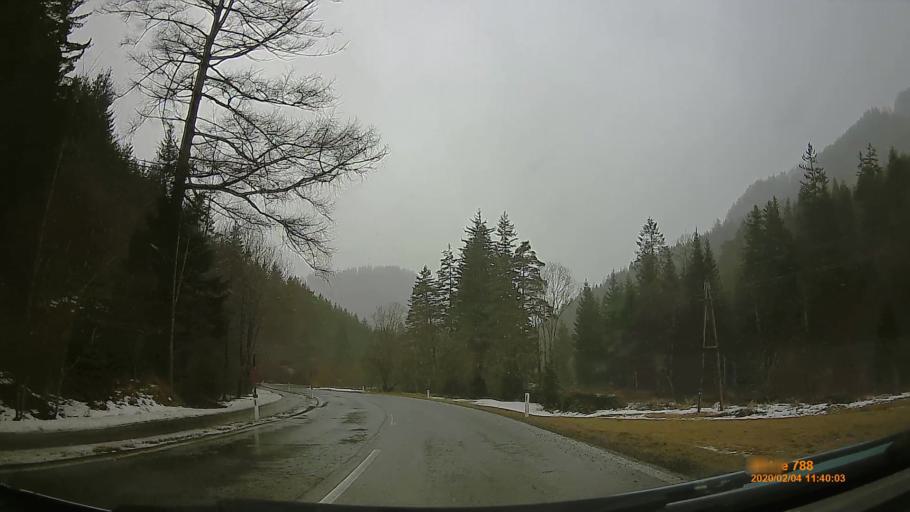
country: AT
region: Styria
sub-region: Politischer Bezirk Bruck-Muerzzuschlag
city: Muerzsteg
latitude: 47.6655
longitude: 15.5154
